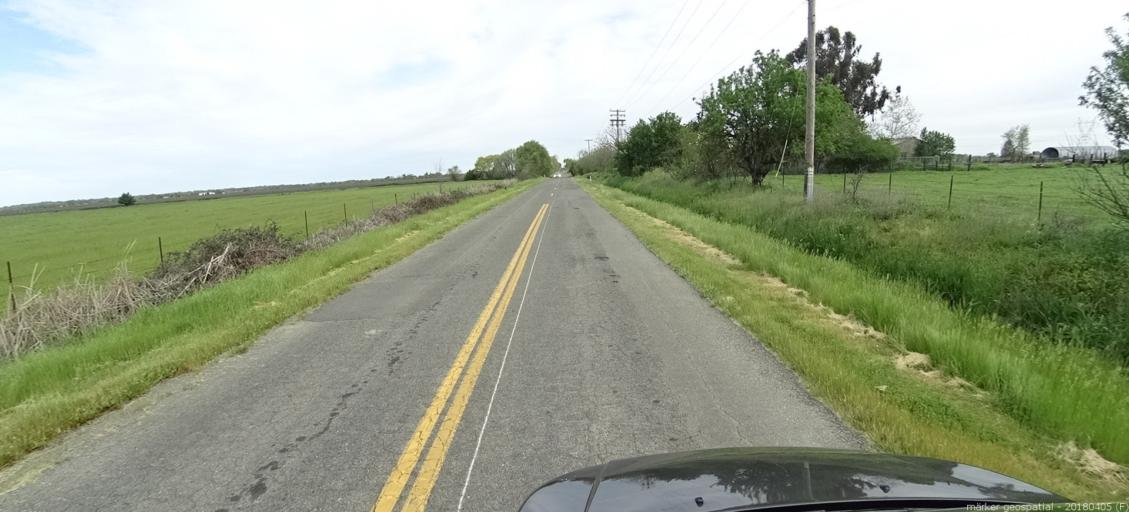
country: US
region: California
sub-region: San Joaquin County
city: Thornton
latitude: 38.2477
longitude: -121.3693
